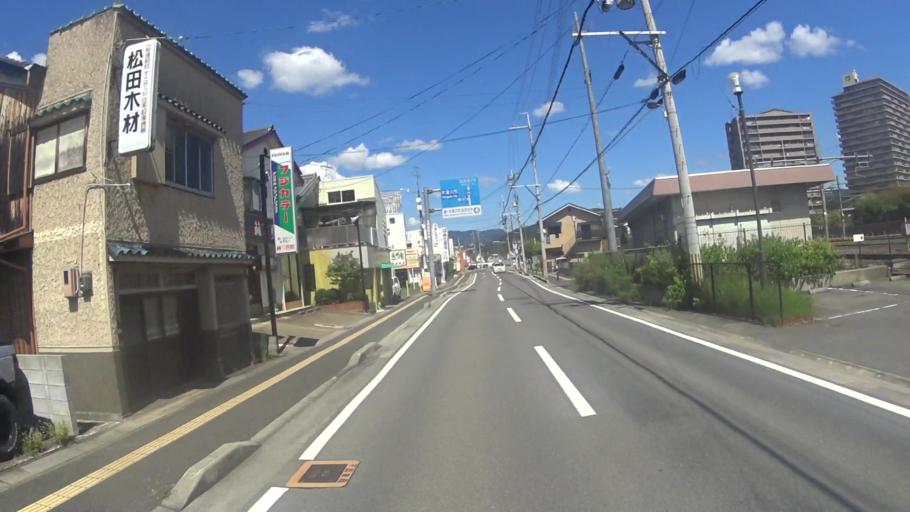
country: JP
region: Kyoto
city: Tanabe
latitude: 34.8646
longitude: 135.7625
